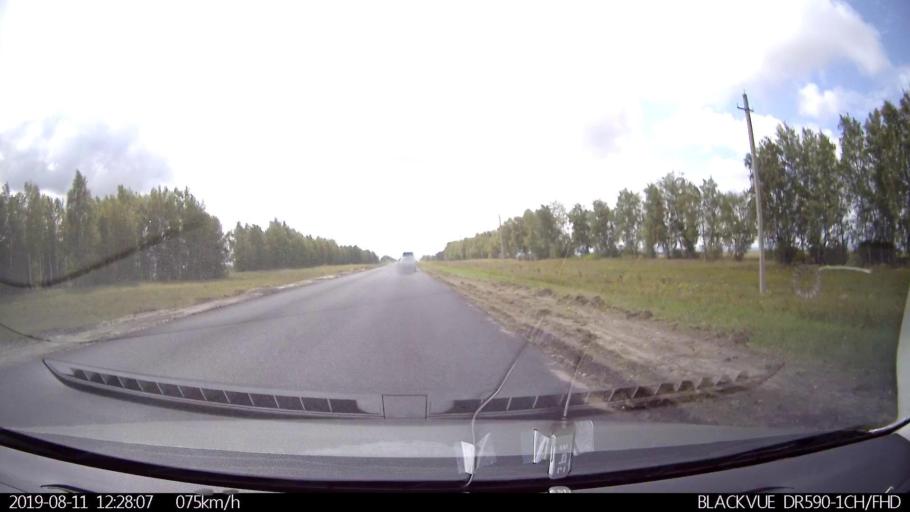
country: RU
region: Ulyanovsk
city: Ignatovka
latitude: 53.8470
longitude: 47.9143
